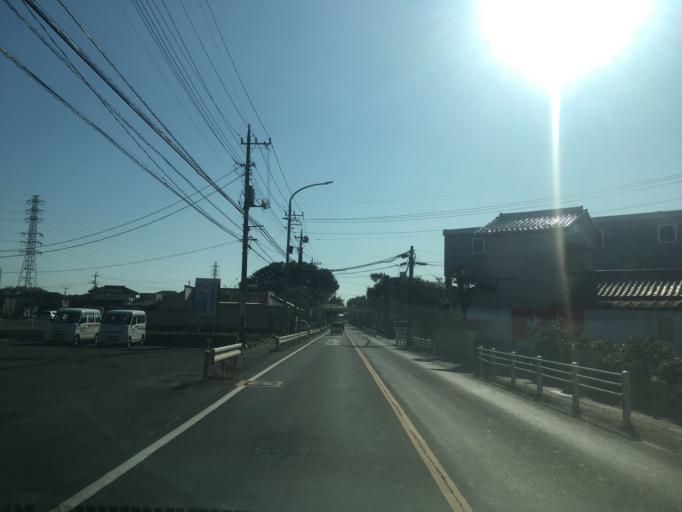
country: JP
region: Saitama
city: Kawagoe
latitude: 35.8751
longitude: 139.4740
